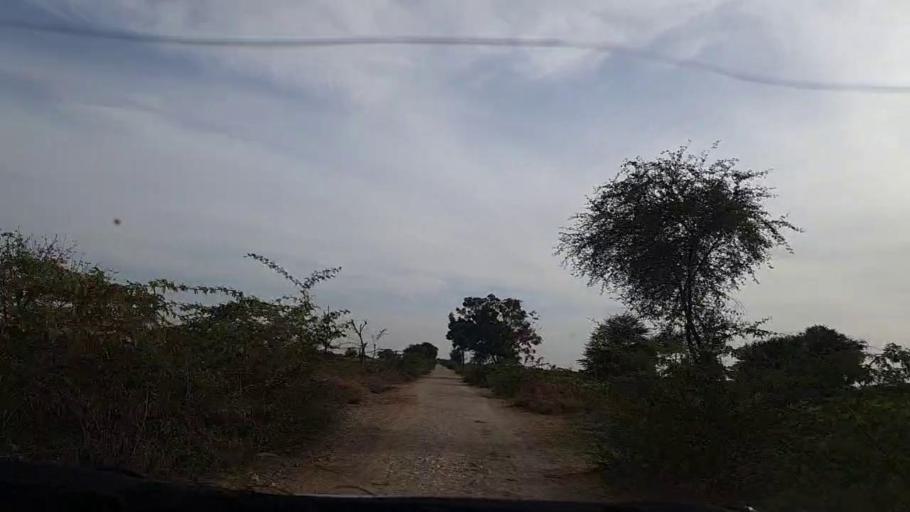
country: PK
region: Sindh
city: Dhoro Naro
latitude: 25.4038
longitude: 69.5178
